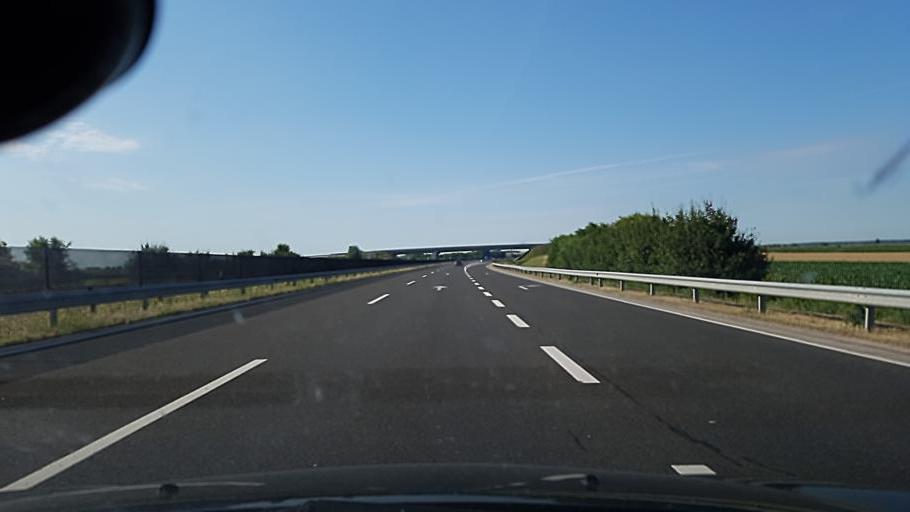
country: HU
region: Fejer
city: dunaujvaros
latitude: 46.9332
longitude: 18.8954
